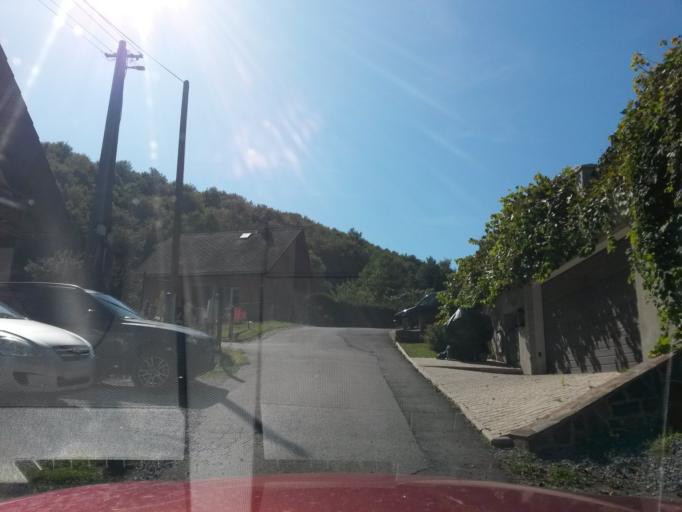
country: SK
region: Presovsky
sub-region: Okres Presov
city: Presov
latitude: 48.9581
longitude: 21.1399
